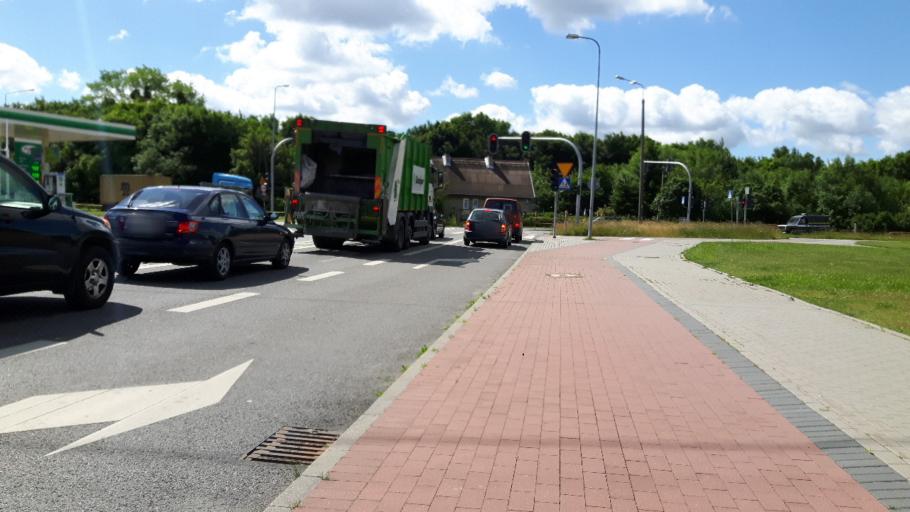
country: PL
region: Pomeranian Voivodeship
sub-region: Gdynia
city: Pogorze
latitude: 54.5643
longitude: 18.5060
